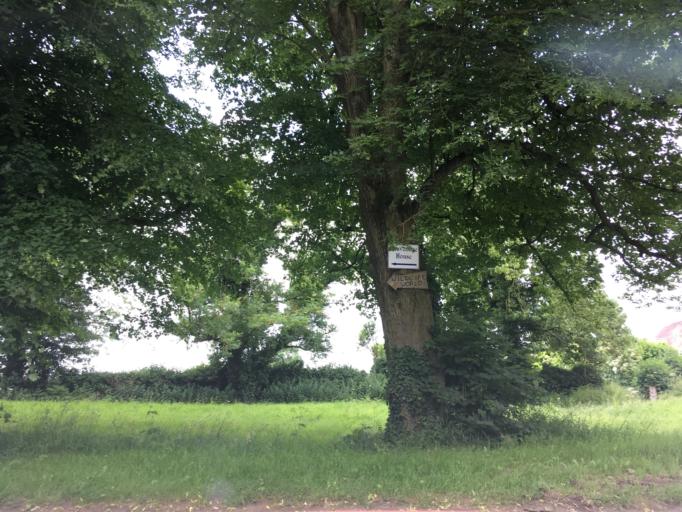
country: GB
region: England
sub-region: Gloucestershire
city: Tetbury
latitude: 51.6588
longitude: -2.1913
